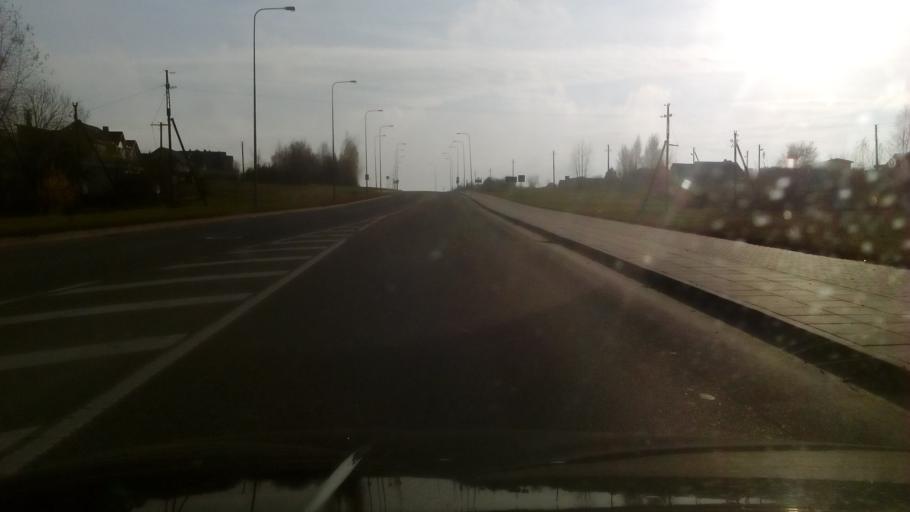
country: LT
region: Alytaus apskritis
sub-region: Alytus
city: Alytus
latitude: 54.3990
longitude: 24.0003
